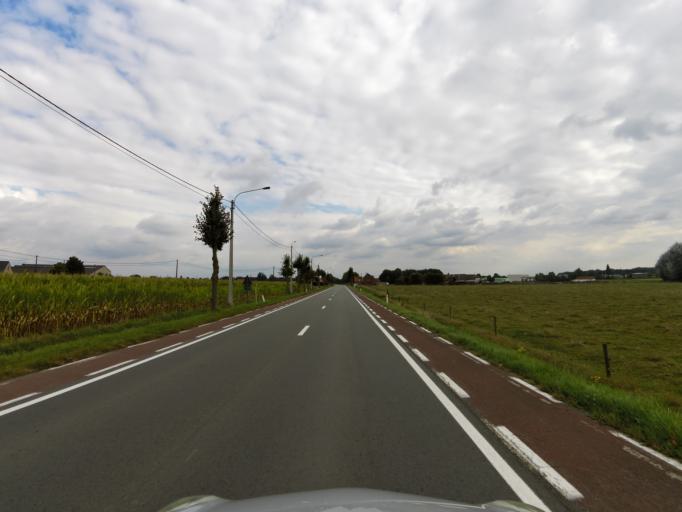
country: BE
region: Flanders
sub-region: Provincie West-Vlaanderen
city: Pittem
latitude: 50.9970
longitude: 3.2420
